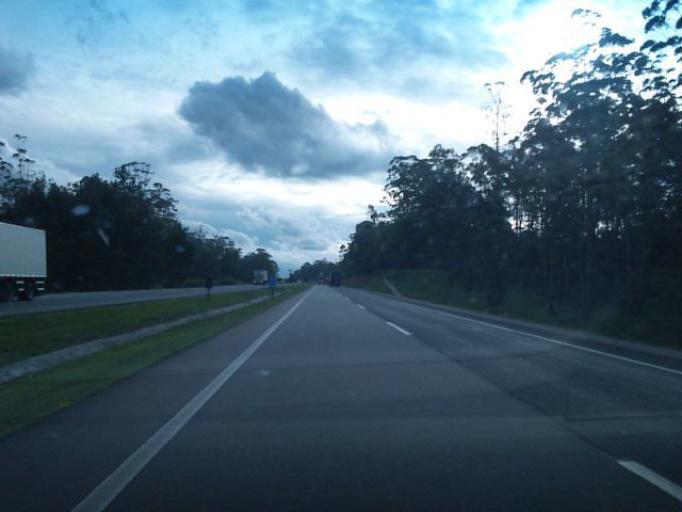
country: BR
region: Parana
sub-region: Piraquara
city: Piraquara
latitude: -25.4298
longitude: -49.0826
